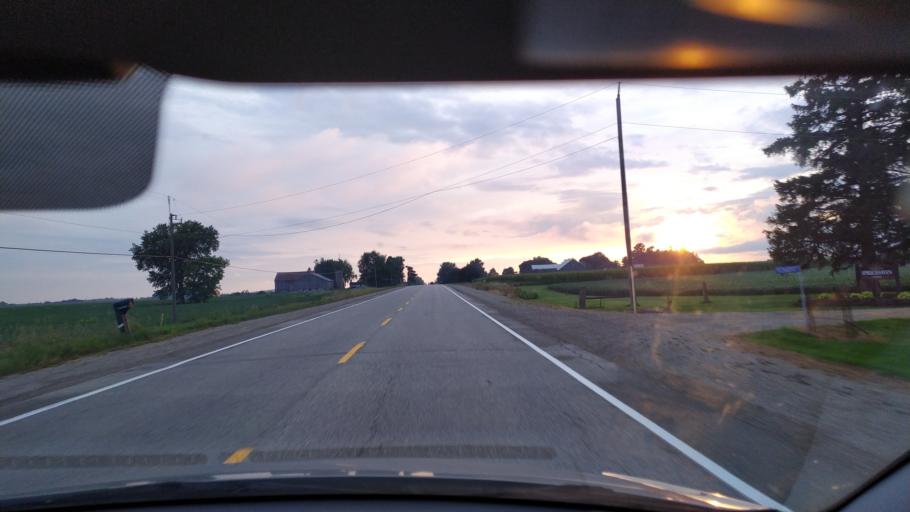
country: CA
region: Ontario
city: Kitchener
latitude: 43.3066
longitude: -80.6005
